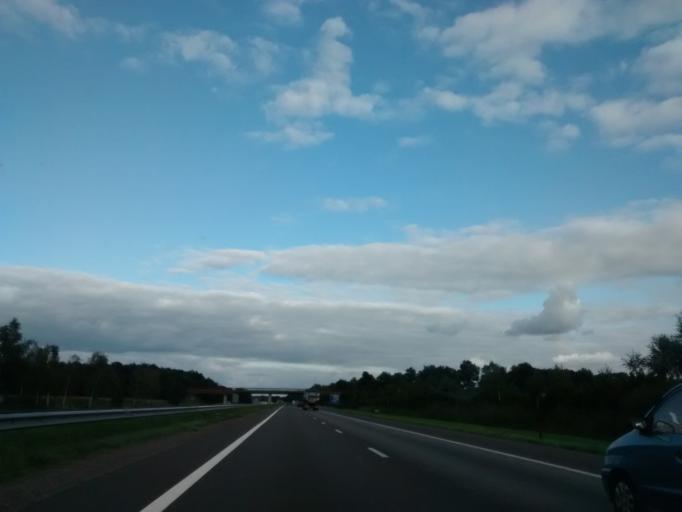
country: NL
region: Gelderland
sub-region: Gemeente Lochem
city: Laren
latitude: 52.2510
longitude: 6.4131
